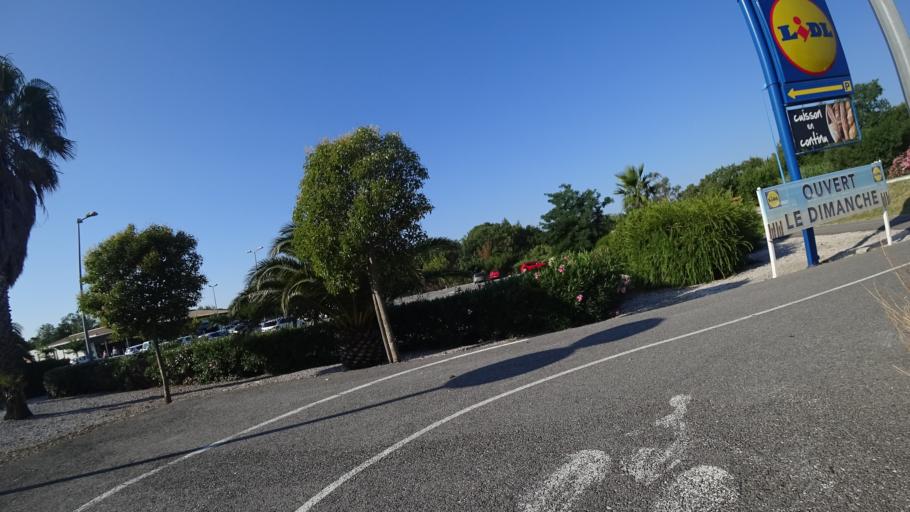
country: FR
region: Languedoc-Roussillon
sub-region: Departement des Pyrenees-Orientales
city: Canet-en-Roussillon
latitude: 42.7000
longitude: 3.0011
